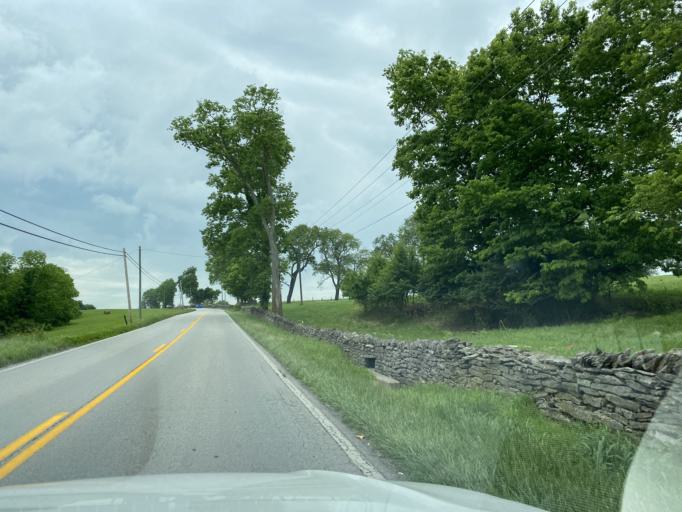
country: US
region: Kentucky
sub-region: Scott County
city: Georgetown
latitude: 38.2211
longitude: -84.5121
